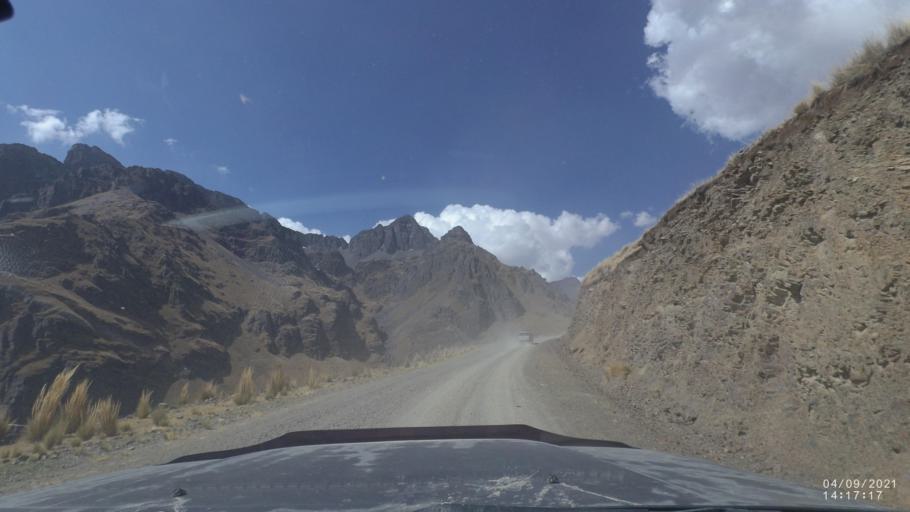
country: BO
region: Cochabamba
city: Sipe Sipe
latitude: -17.2304
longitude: -66.4356
